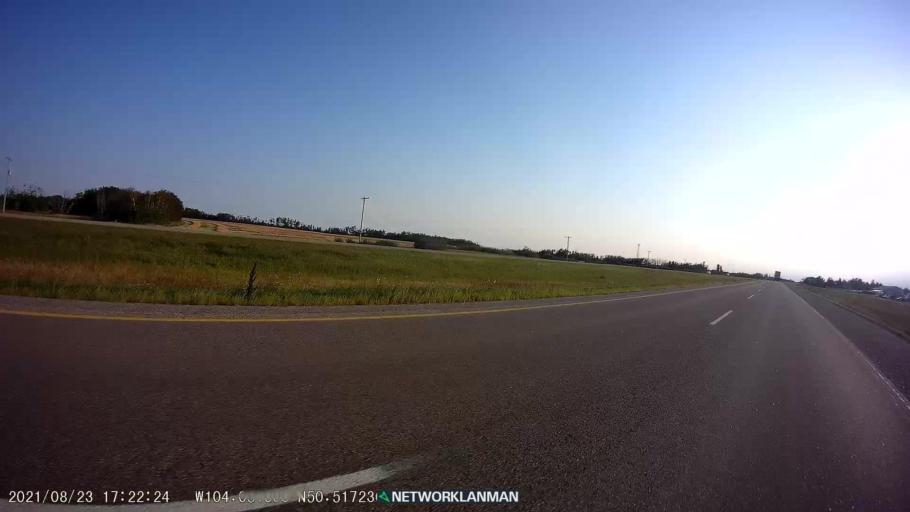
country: CA
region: Saskatchewan
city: White City
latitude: 50.5168
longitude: -104.0503
